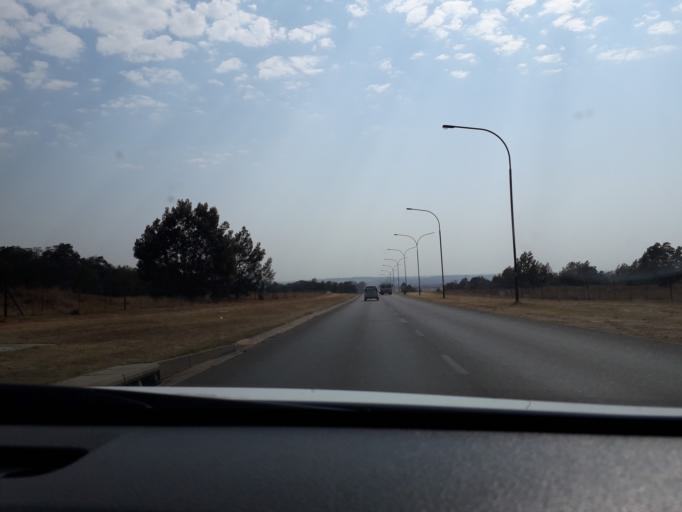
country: ZA
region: Gauteng
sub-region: Ekurhuleni Metropolitan Municipality
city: Tembisa
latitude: -26.0661
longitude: 28.2662
